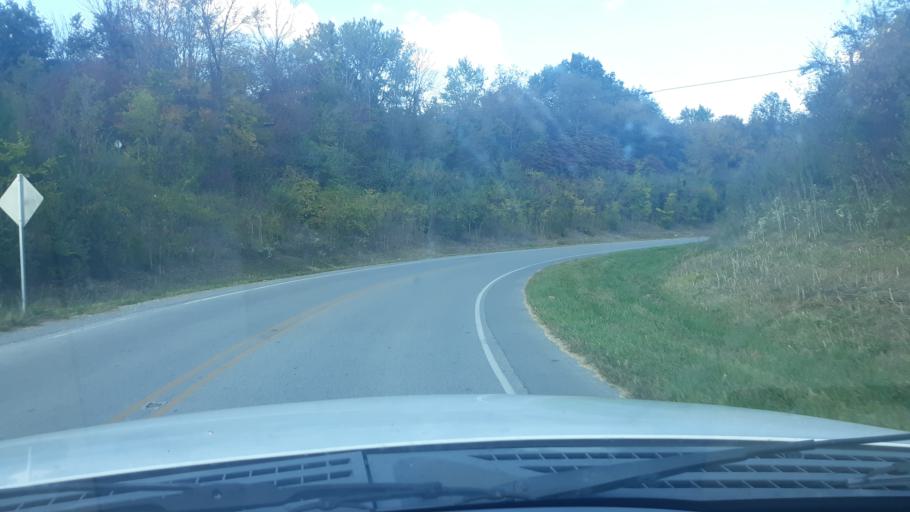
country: US
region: Illinois
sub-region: Saline County
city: Eldorado
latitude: 37.7878
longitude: -88.4863
